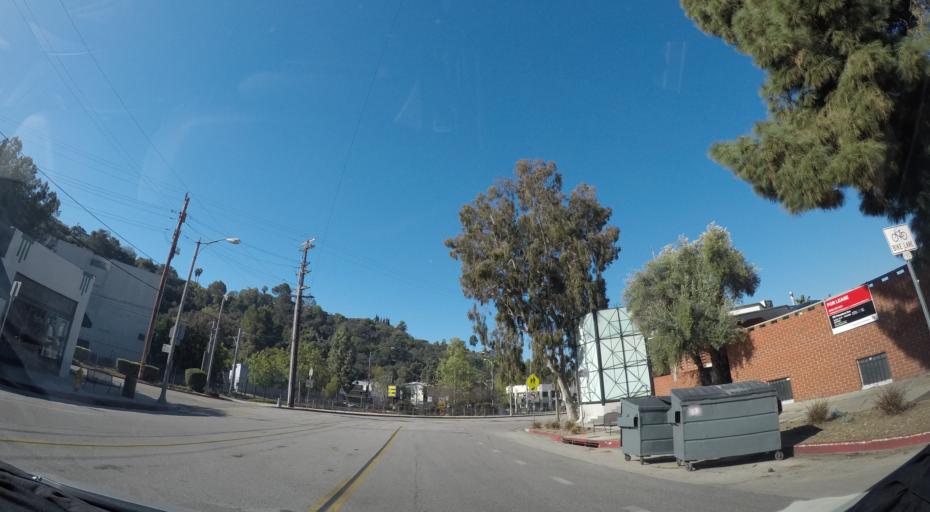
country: US
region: California
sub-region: Los Angeles County
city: South Pasadena
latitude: 34.1125
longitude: -118.1691
